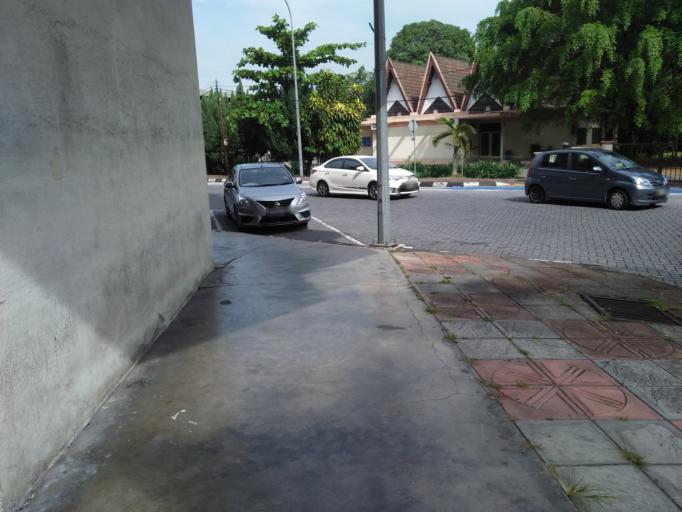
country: MY
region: Perak
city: Ipoh
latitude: 4.6013
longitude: 101.0857
